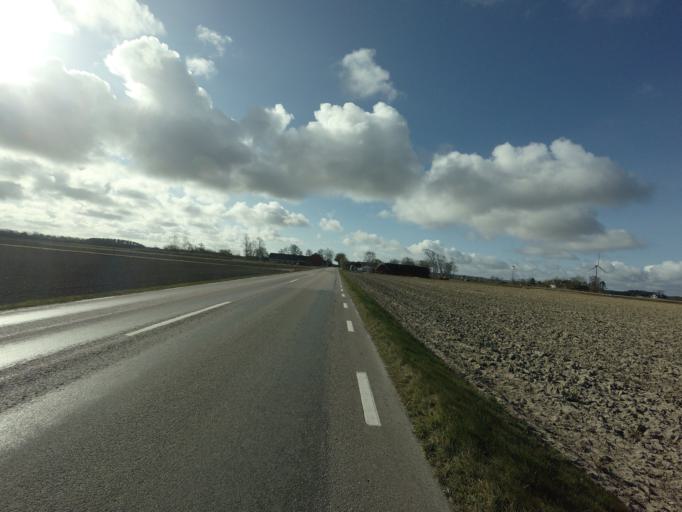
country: SE
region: Skane
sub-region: Helsingborg
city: Odakra
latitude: 56.1620
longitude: 12.6783
